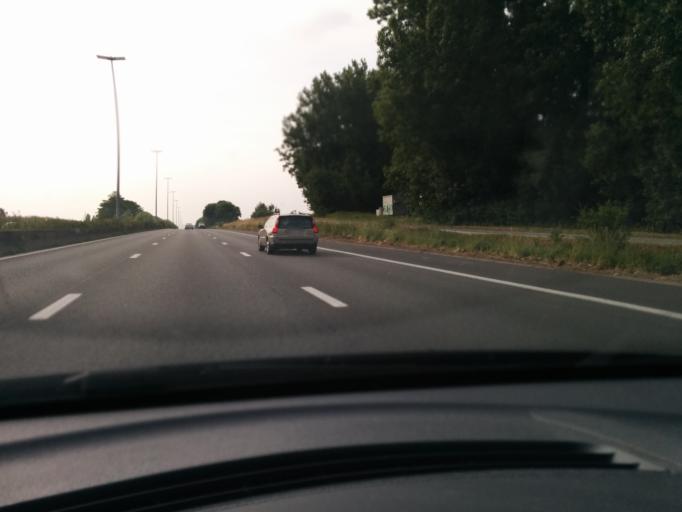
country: BE
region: Flanders
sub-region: Provincie Oost-Vlaanderen
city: Sint-Lievens-Houtem
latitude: 50.9404
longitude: 3.9154
